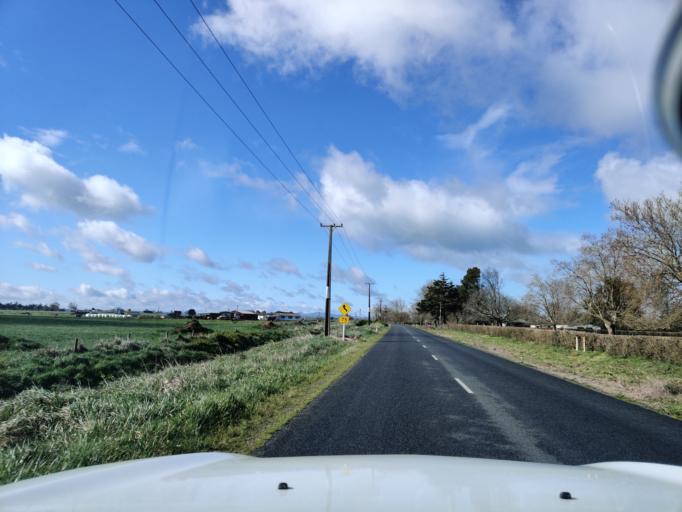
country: NZ
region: Waikato
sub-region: Waikato District
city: Ngaruawahia
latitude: -37.6142
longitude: 175.3132
